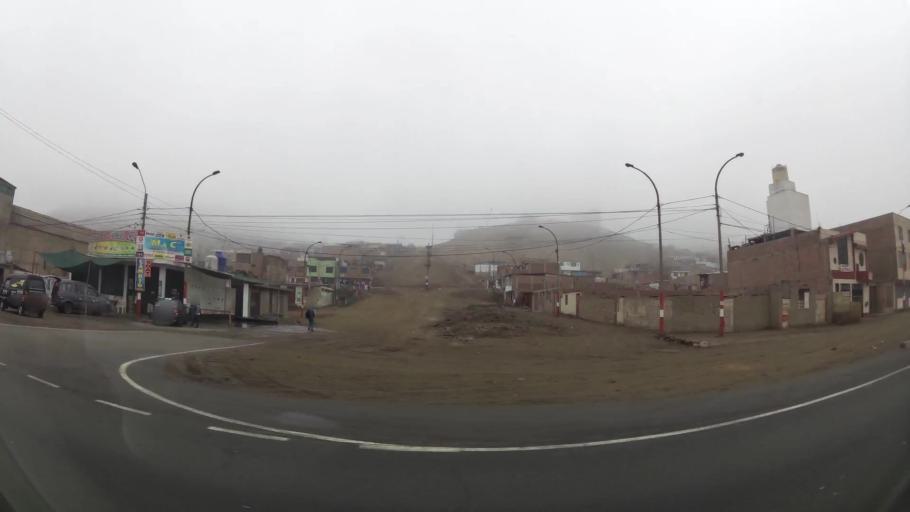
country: PE
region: Lima
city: Ventanilla
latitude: -11.8440
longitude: -77.1173
